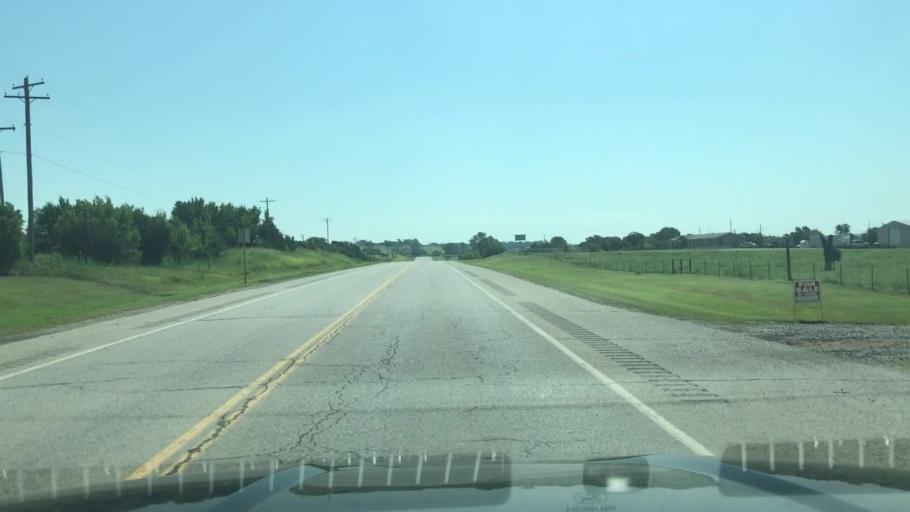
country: US
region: Oklahoma
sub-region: Creek County
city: Drumright
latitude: 35.9884
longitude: -96.5615
